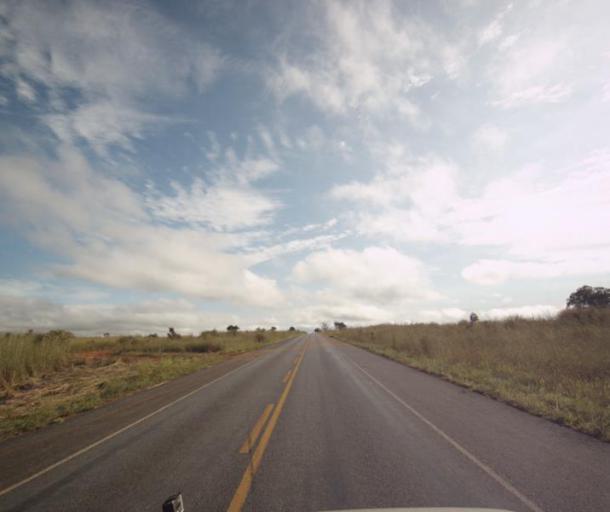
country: BR
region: Goias
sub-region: Padre Bernardo
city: Padre Bernardo
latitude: -15.4700
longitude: -48.6145
